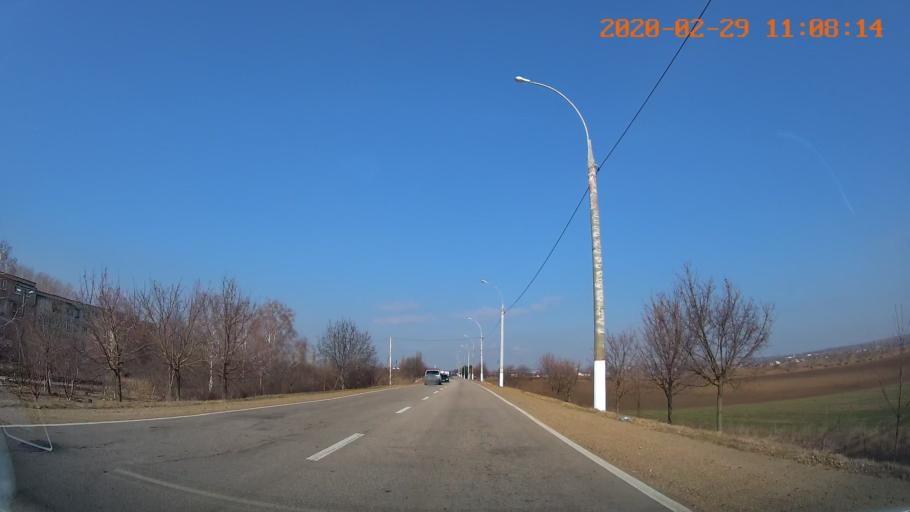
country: MD
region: Criuleni
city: Criuleni
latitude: 47.2321
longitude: 29.1770
